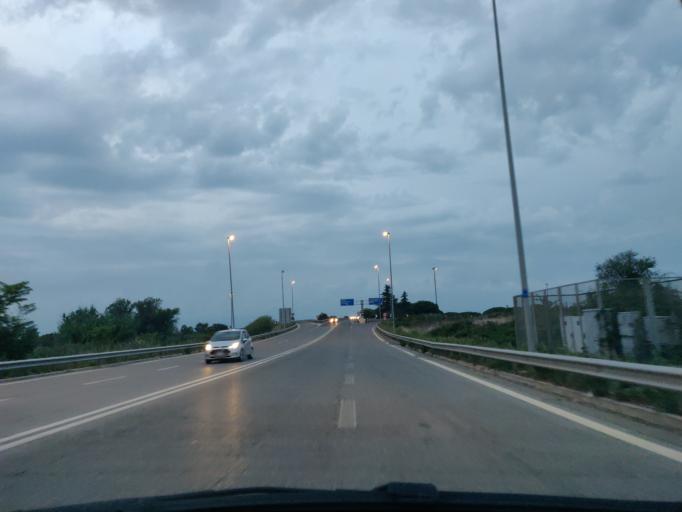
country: IT
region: Latium
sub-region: Provincia di Viterbo
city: Vetralla
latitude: 42.3724
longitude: 12.0548
